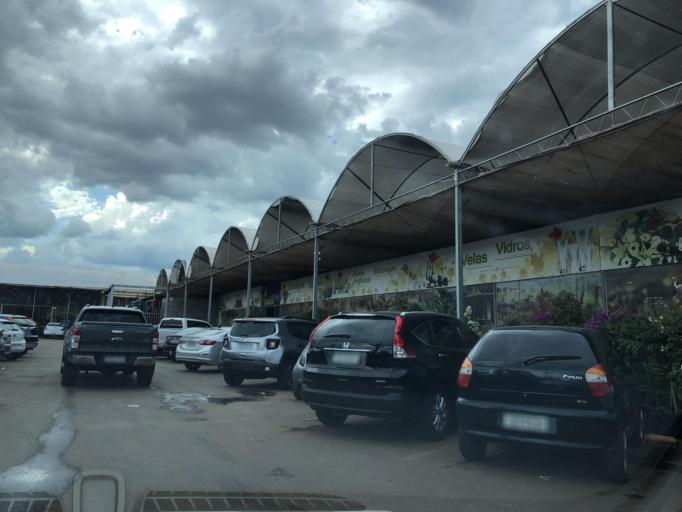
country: BR
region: Federal District
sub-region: Brasilia
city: Brasilia
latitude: -15.8139
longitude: -48.0090
